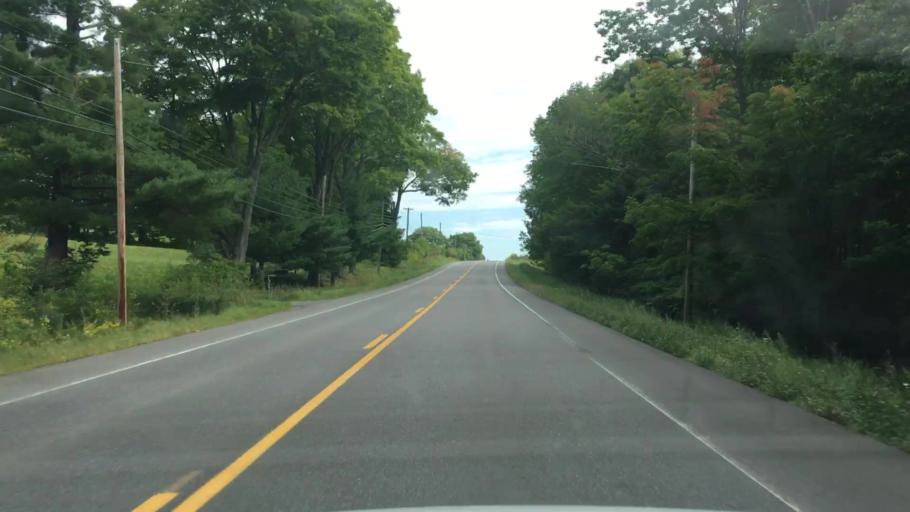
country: US
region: Maine
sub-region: Piscataquis County
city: Brownville
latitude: 45.2275
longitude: -69.1103
